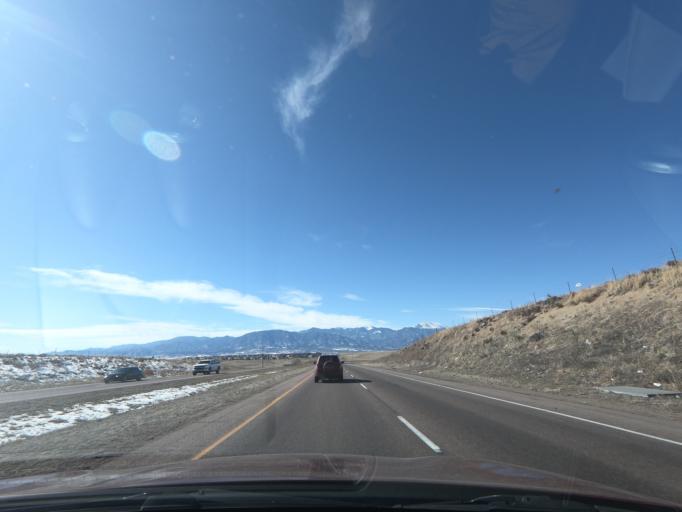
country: US
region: Colorado
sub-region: El Paso County
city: Security-Widefield
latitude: 38.7662
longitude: -104.6901
